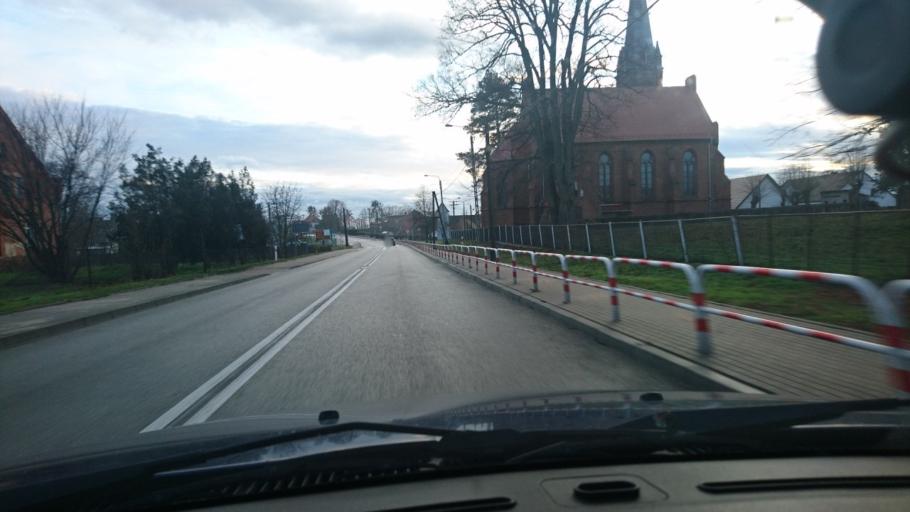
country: PL
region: Opole Voivodeship
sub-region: Powiat kluczborski
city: Kluczbork
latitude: 51.0292
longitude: 18.1920
